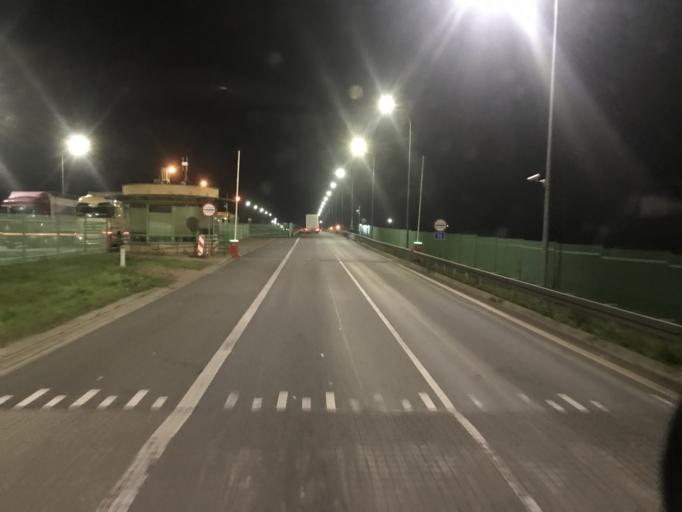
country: PL
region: Lublin Voivodeship
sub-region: Powiat bialski
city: Terespol
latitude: 52.1144
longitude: 23.5645
